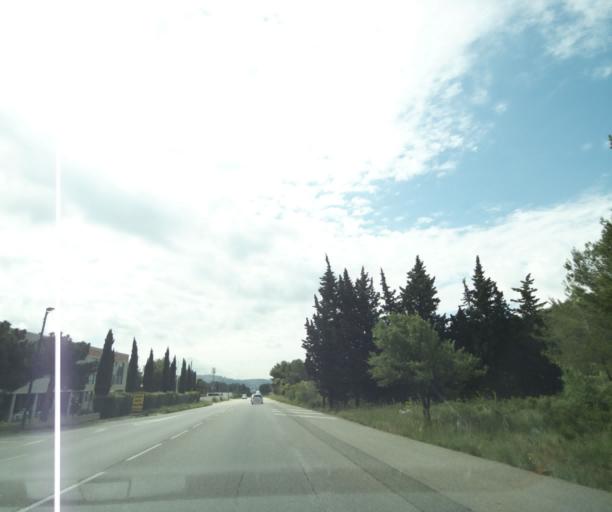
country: FR
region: Provence-Alpes-Cote d'Azur
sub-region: Departement des Bouches-du-Rhone
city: Rognac
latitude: 43.5096
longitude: 5.2056
